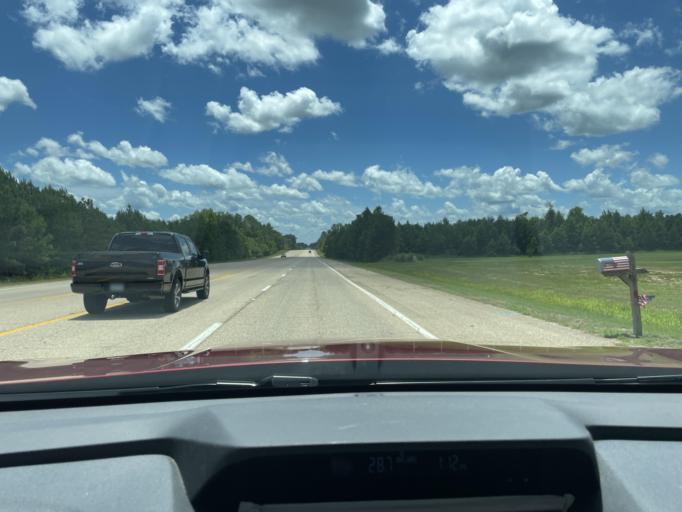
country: US
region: Arkansas
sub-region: Drew County
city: Monticello
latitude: 33.6851
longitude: -91.8057
